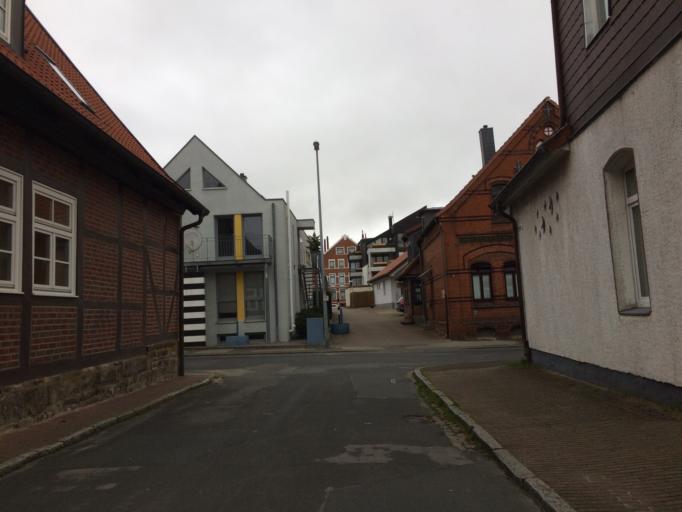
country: DE
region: Lower Saxony
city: Gehrden
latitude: 52.3141
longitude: 9.6017
